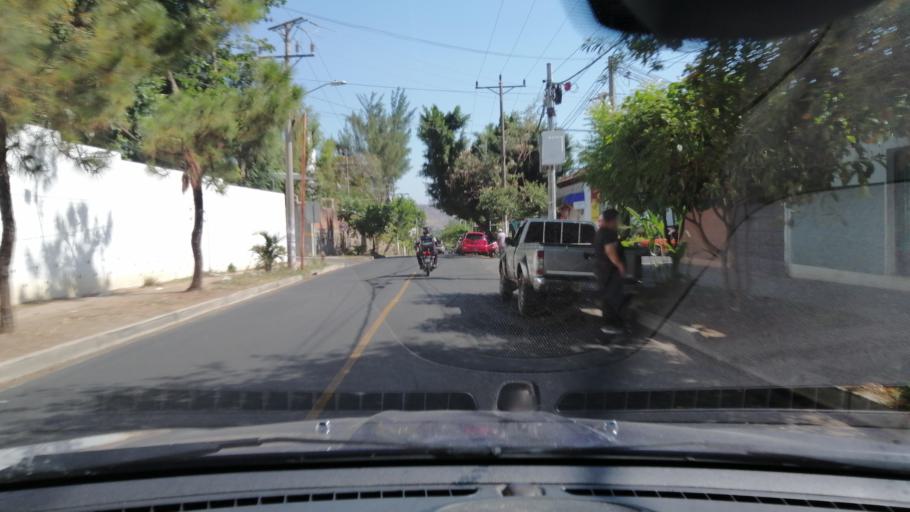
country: SV
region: Santa Ana
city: Santa Ana
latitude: 13.9908
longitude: -89.5506
